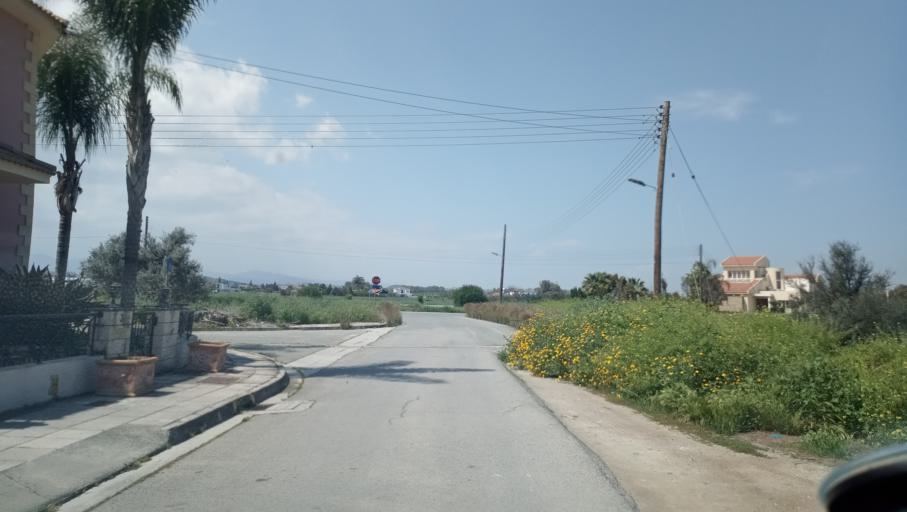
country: CY
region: Lefkosia
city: Dali
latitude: 35.0199
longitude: 33.4094
